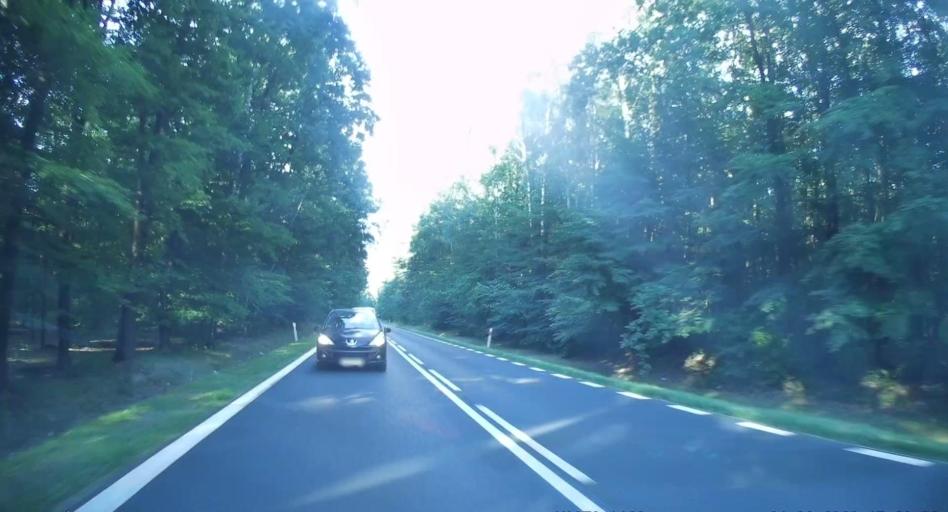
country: PL
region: Lodz Voivodeship
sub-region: Powiat rawski
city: Rawa Mazowiecka
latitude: 51.7781
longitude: 20.3028
